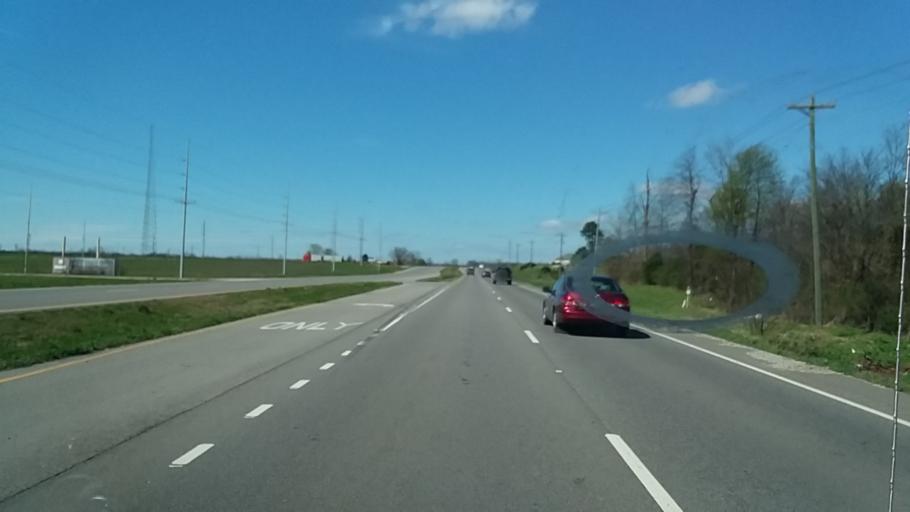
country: US
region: Alabama
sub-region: Morgan County
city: Trinity
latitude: 34.6348
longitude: -87.1091
